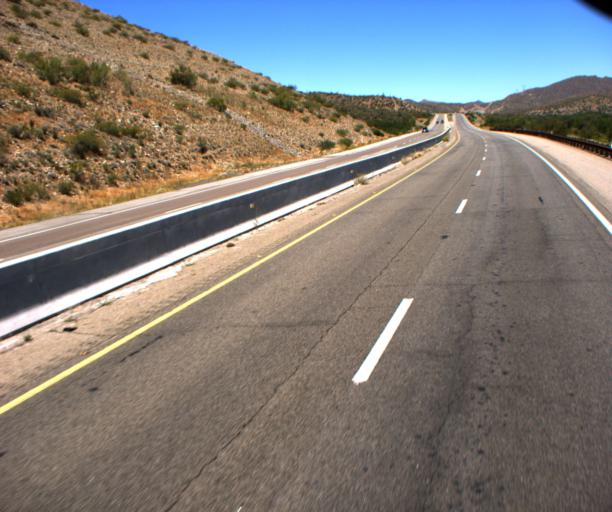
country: US
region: Arizona
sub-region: Yavapai County
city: Bagdad
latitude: 34.3798
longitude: -113.1935
